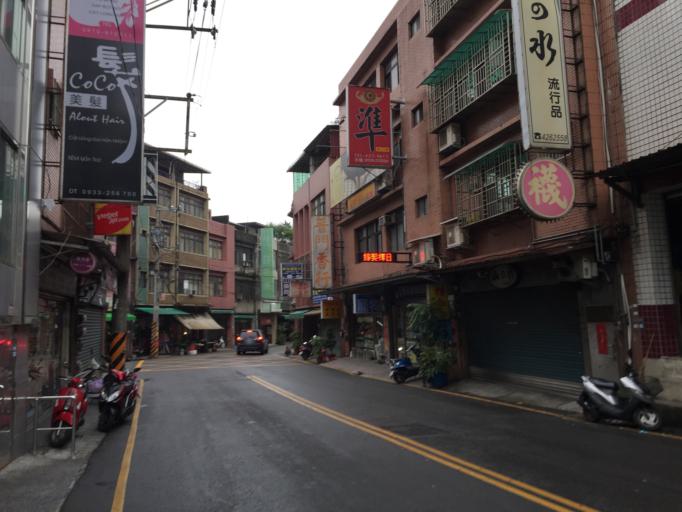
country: TW
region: Taiwan
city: Taoyuan City
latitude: 24.9556
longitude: 121.2280
